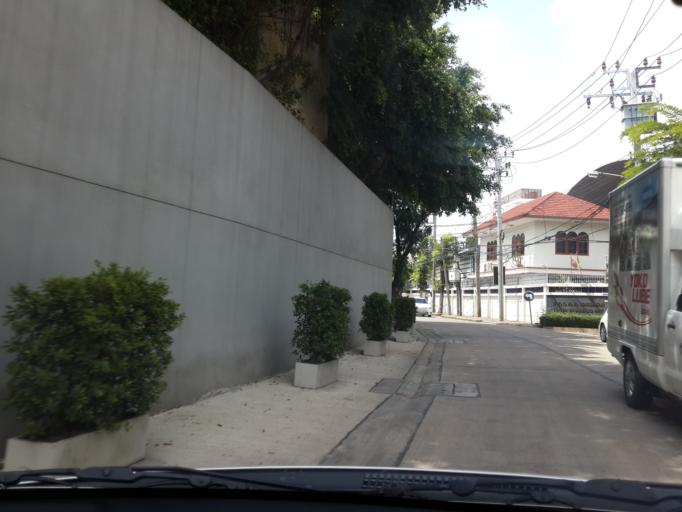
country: TH
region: Bangkok
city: Lak Si
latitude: 13.8744
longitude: 100.5836
